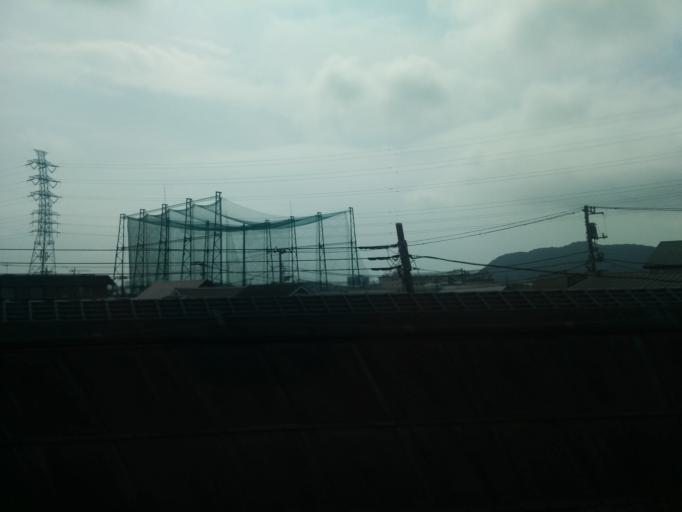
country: JP
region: Kanagawa
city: Hiratsuka
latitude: 35.3444
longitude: 139.3095
